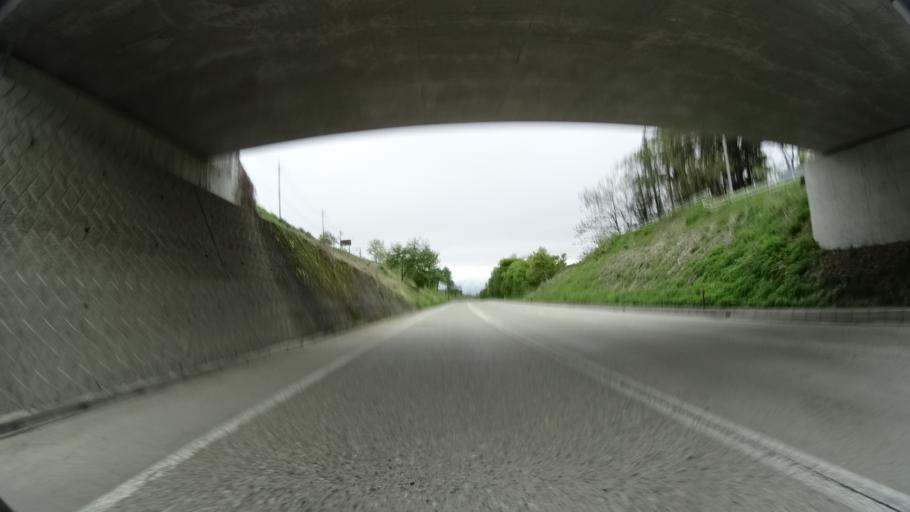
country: JP
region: Nagano
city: Nakano
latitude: 36.7297
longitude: 138.4238
